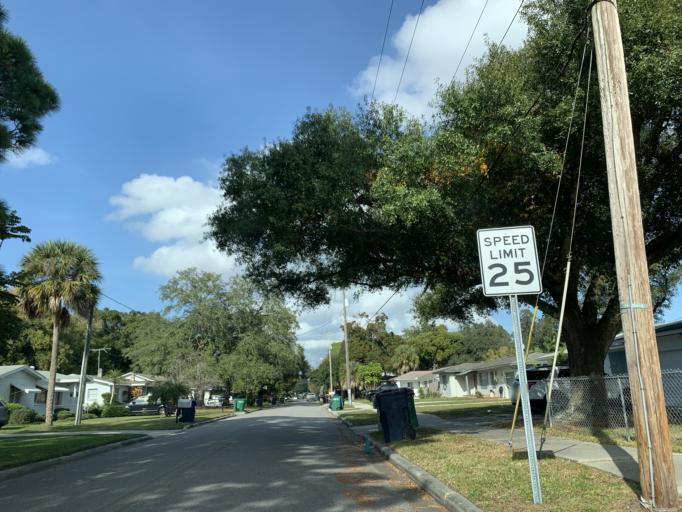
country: US
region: Florida
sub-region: Hillsborough County
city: Tampa
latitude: 27.9091
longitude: -82.5143
